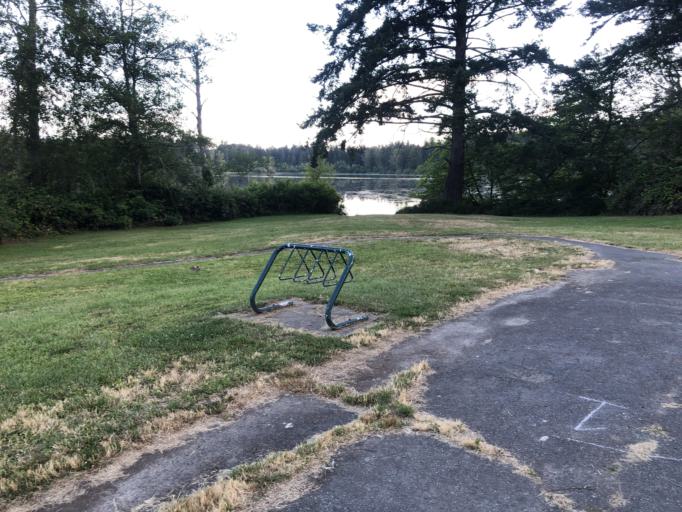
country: CA
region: British Columbia
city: Victoria
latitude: 48.5097
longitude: -123.3911
